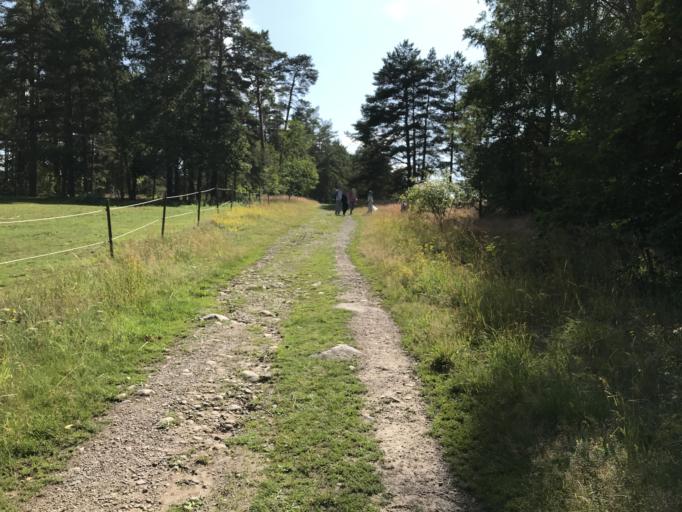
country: SE
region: OEstergoetland
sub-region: Norrkopings Kommun
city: Norrkoping
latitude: 58.5690
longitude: 16.1969
